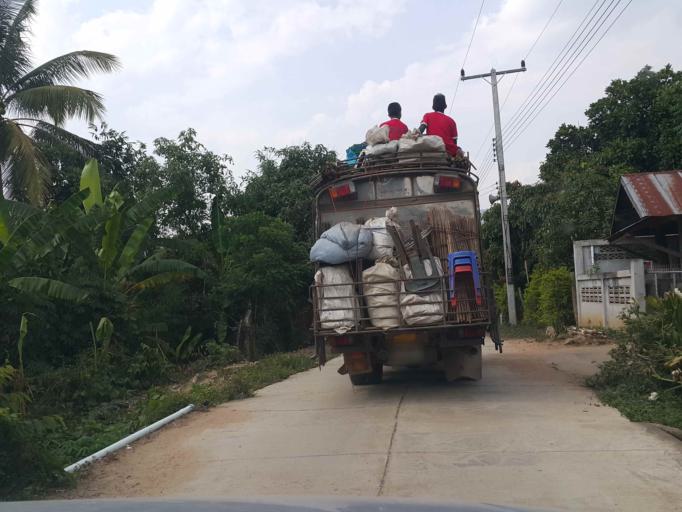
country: TH
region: Chiang Mai
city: Wiang Haeng
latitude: 19.3973
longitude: 98.7222
